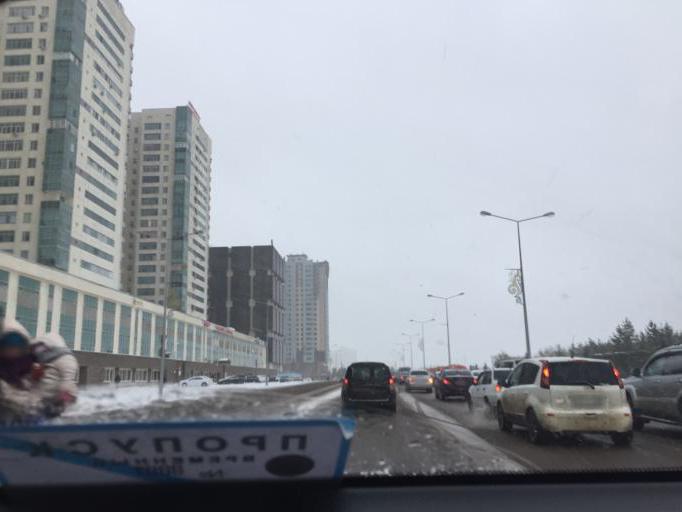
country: KZ
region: Astana Qalasy
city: Astana
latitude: 51.1325
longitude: 71.4593
